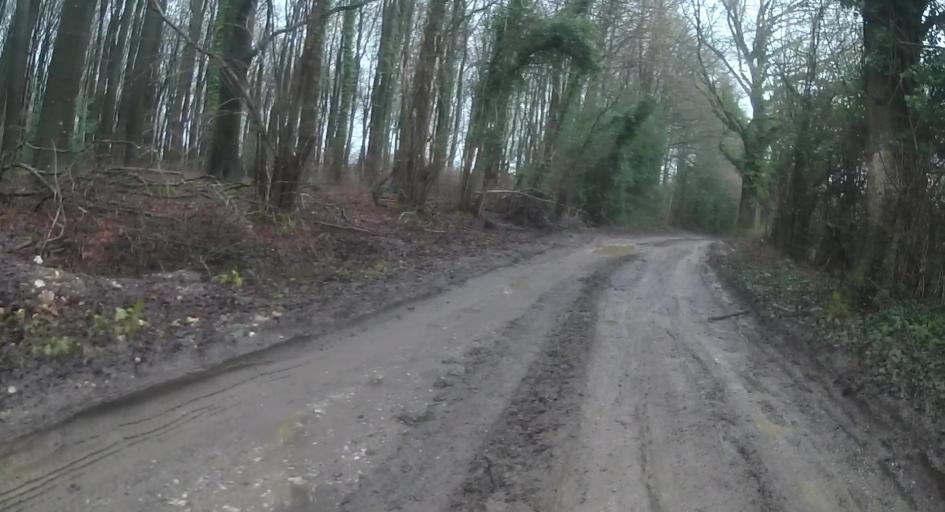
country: GB
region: England
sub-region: Hampshire
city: Kings Worthy
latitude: 51.1140
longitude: -1.2528
